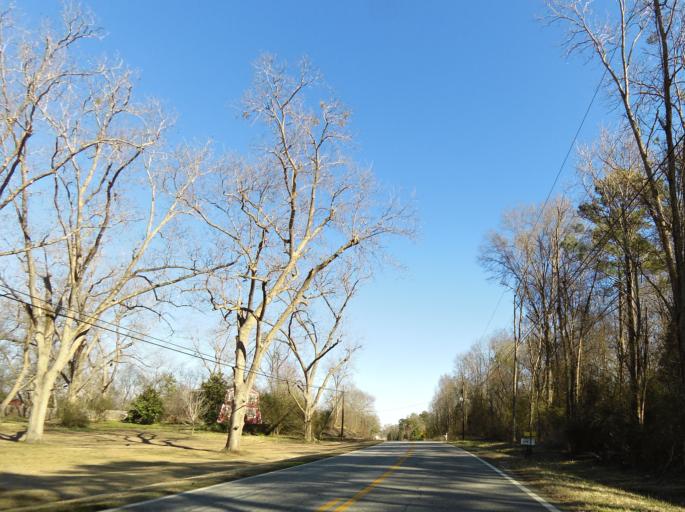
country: US
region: Georgia
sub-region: Bibb County
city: West Point
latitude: 32.8316
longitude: -83.8318
